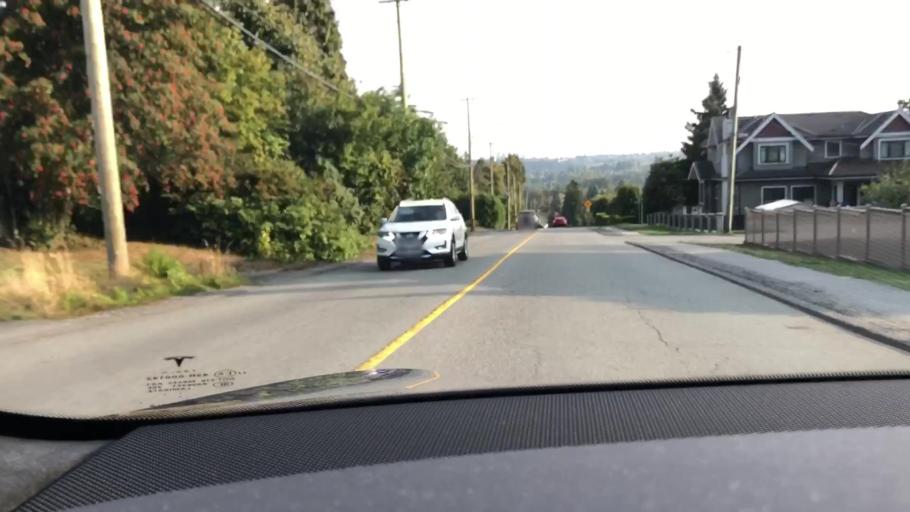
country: CA
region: British Columbia
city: Burnaby
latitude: 49.2670
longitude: -122.9702
